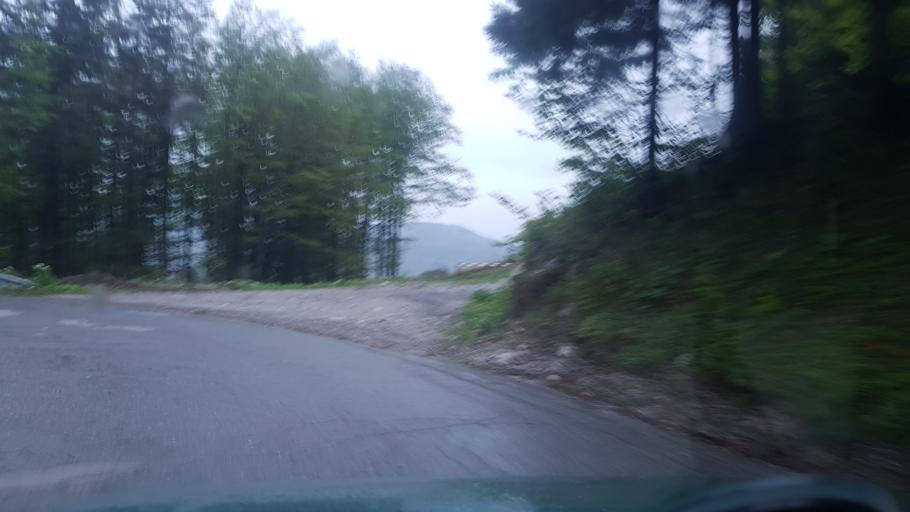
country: SI
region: Bohinj
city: Bohinjska Bistrica
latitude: 46.2285
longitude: 14.0234
